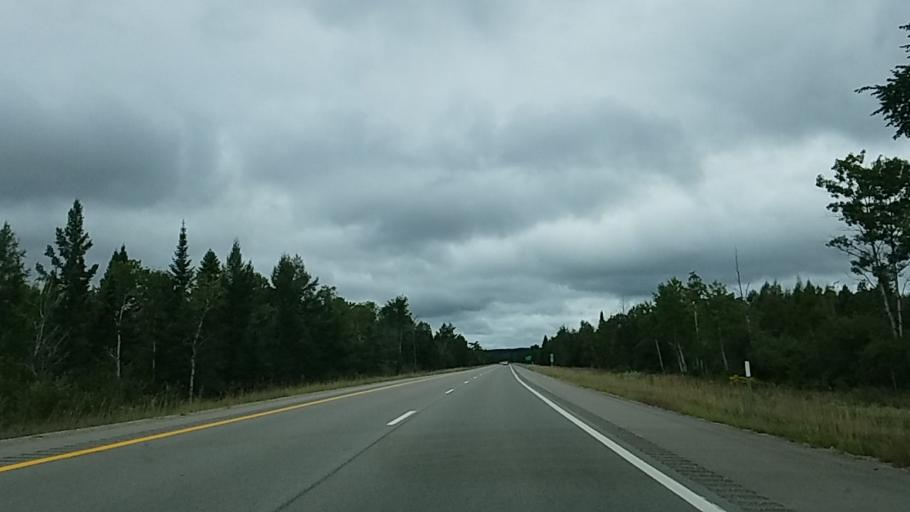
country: US
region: Michigan
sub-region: Otsego County
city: Gaylord
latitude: 45.1689
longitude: -84.6489
